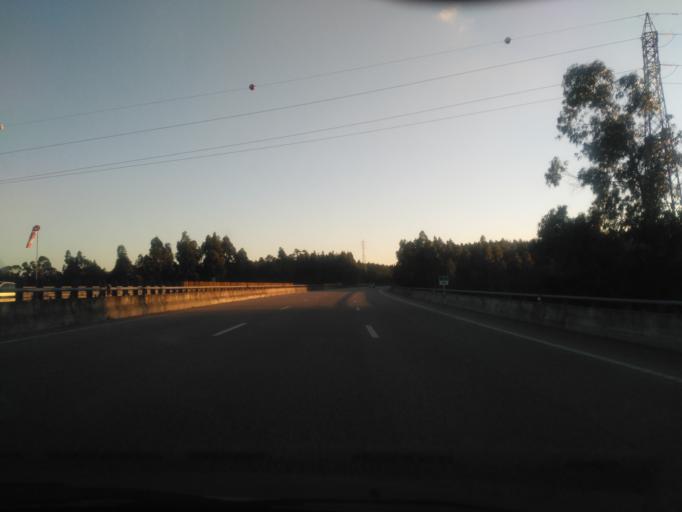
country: PT
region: Leiria
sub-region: Leiria
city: Maceira
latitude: 39.7273
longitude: -8.8941
